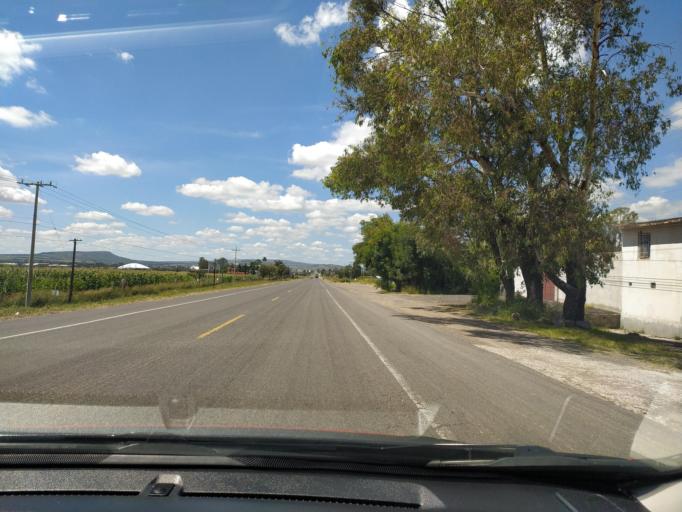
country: MX
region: Jalisco
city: San Miguel el Alto
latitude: 21.0206
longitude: -102.3497
